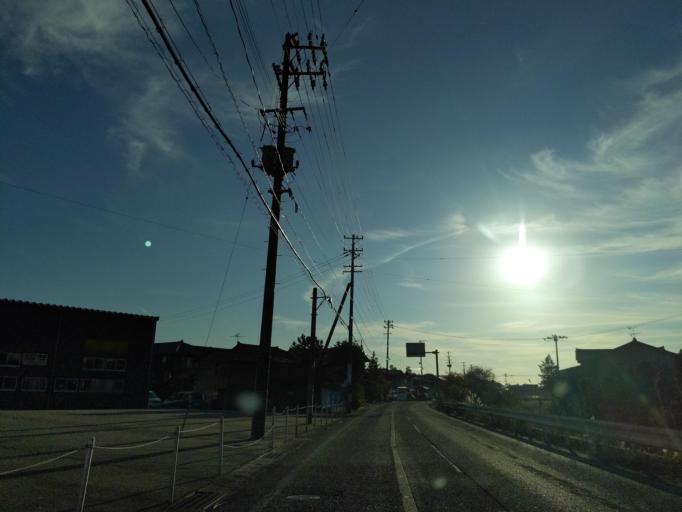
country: JP
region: Niigata
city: Nagaoka
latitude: 37.5801
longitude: 138.7709
